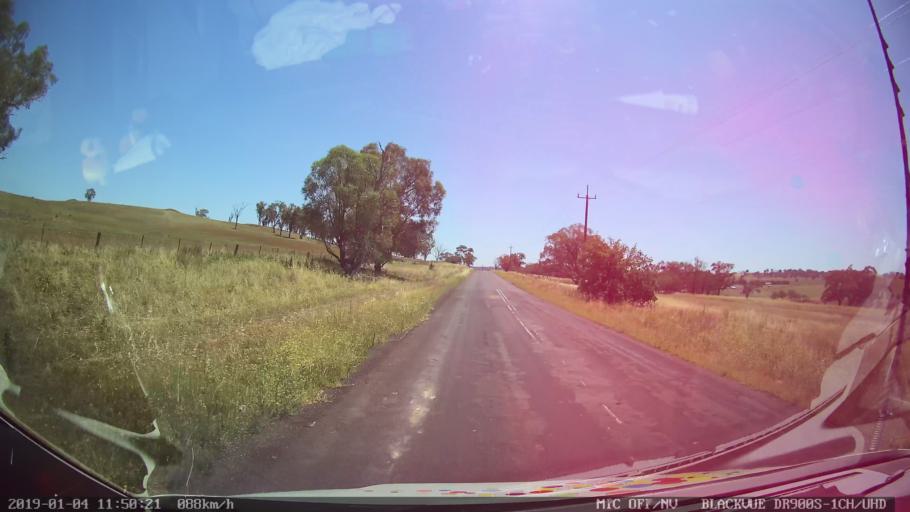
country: AU
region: New South Wales
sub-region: Cabonne
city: Molong
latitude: -32.9073
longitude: 148.7562
